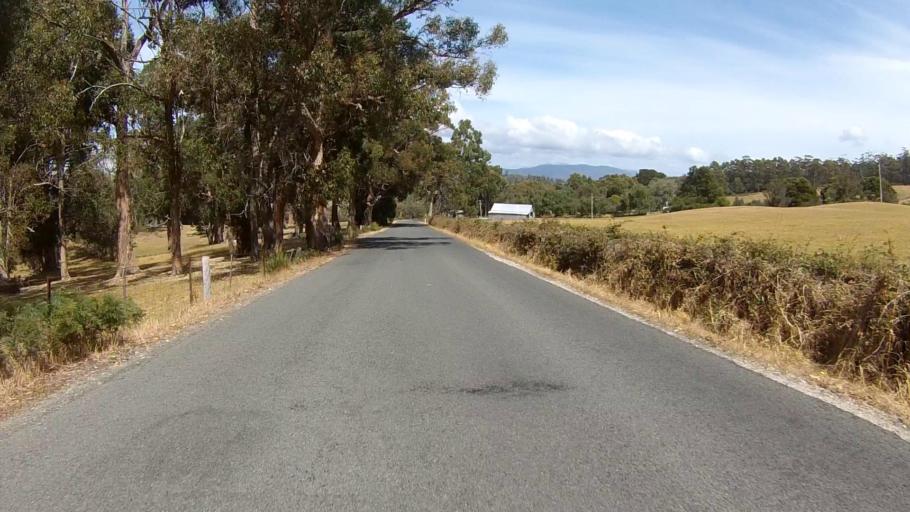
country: AU
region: Tasmania
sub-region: Huon Valley
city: Cygnet
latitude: -43.2323
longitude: 147.1294
